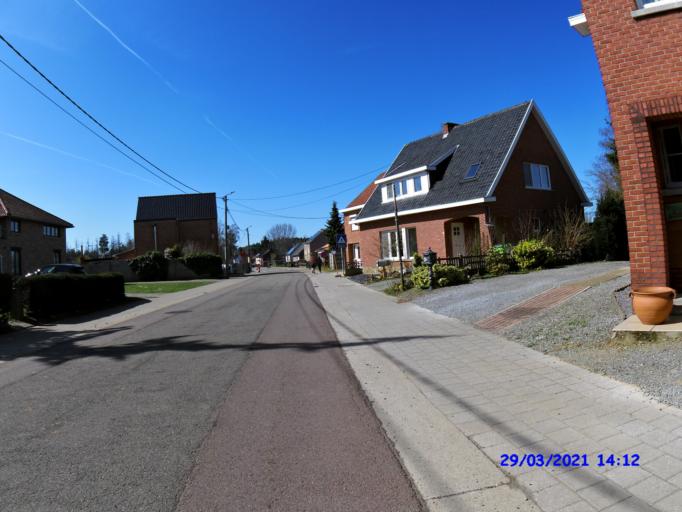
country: BE
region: Flanders
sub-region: Provincie Vlaams-Brabant
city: Bekkevoort
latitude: 50.9467
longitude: 4.9774
